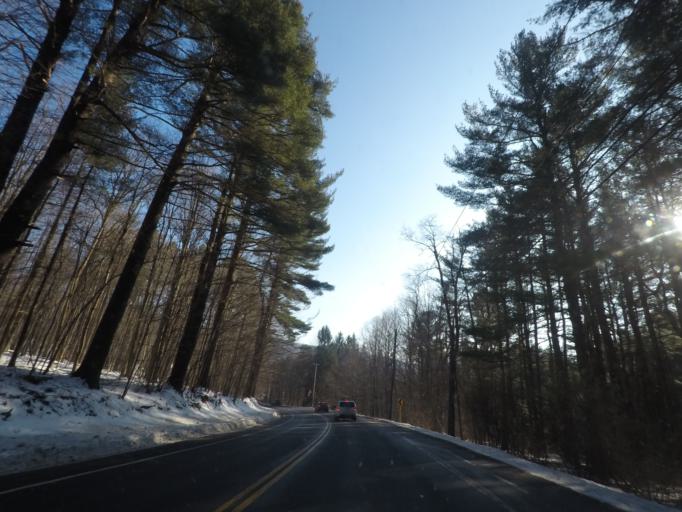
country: US
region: Massachusetts
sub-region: Berkshire County
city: Richmond
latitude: 42.4827
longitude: -73.3743
